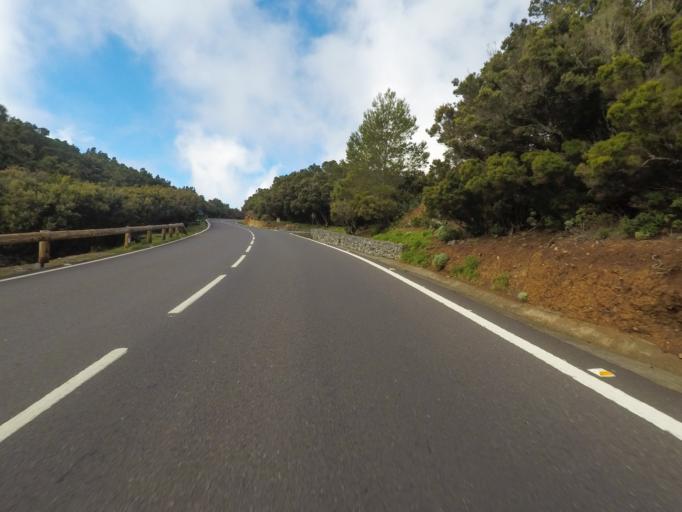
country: ES
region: Canary Islands
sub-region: Provincia de Santa Cruz de Tenerife
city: Alajero
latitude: 28.0993
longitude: -17.1957
